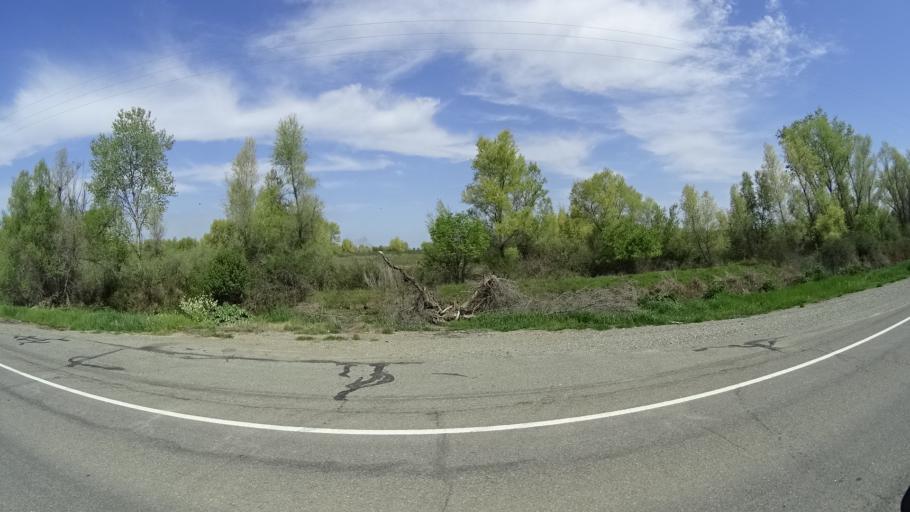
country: US
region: California
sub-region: Butte County
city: Biggs
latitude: 39.4640
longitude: -121.8802
